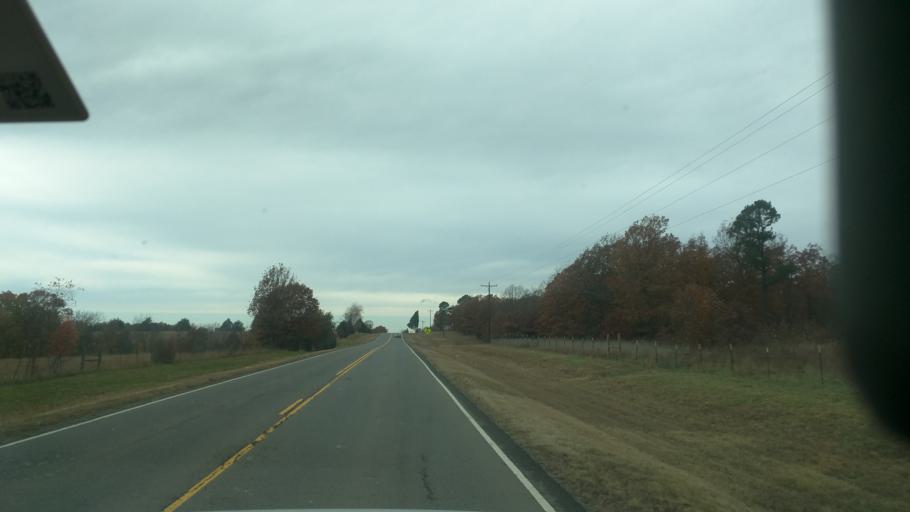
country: US
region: Oklahoma
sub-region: Cherokee County
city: Park Hill
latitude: 35.8986
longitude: -94.7981
